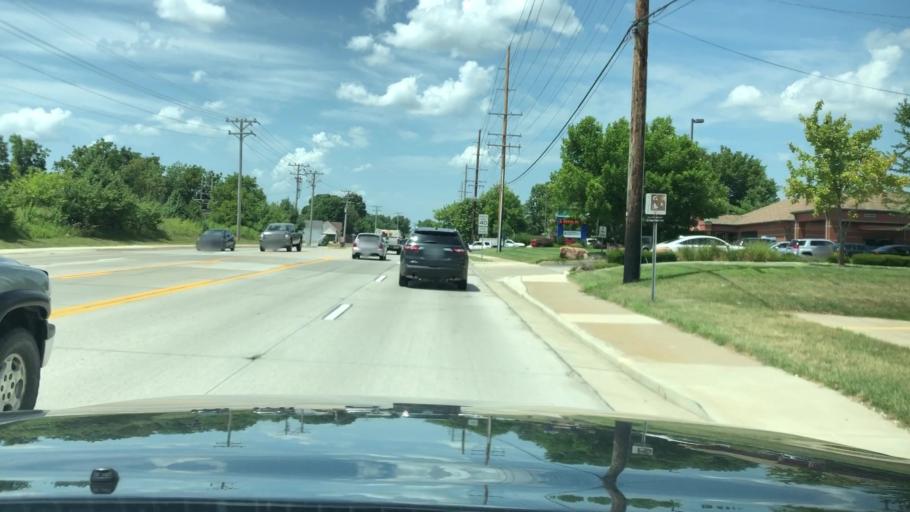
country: US
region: Missouri
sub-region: Saint Charles County
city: Saint Peters
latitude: 38.7873
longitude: -90.6630
